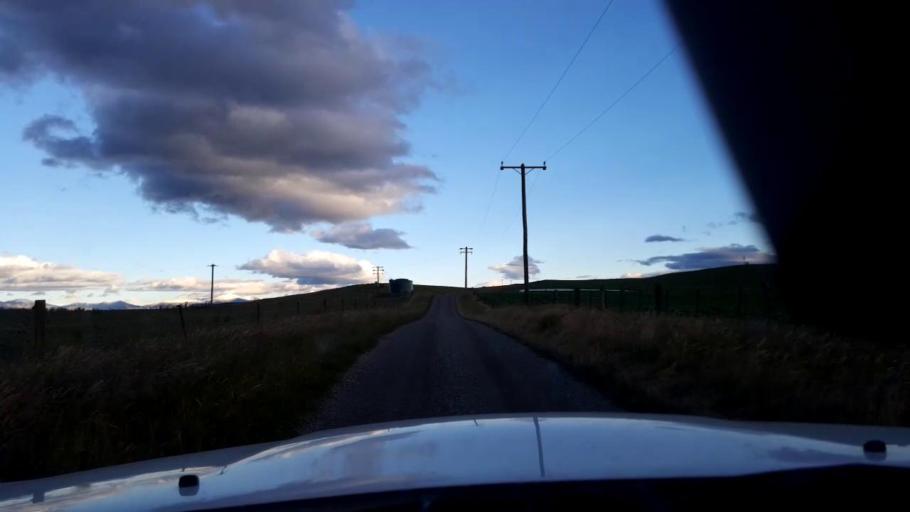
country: NZ
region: Canterbury
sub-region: Timaru District
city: Pleasant Point
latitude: -44.2473
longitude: 170.9084
